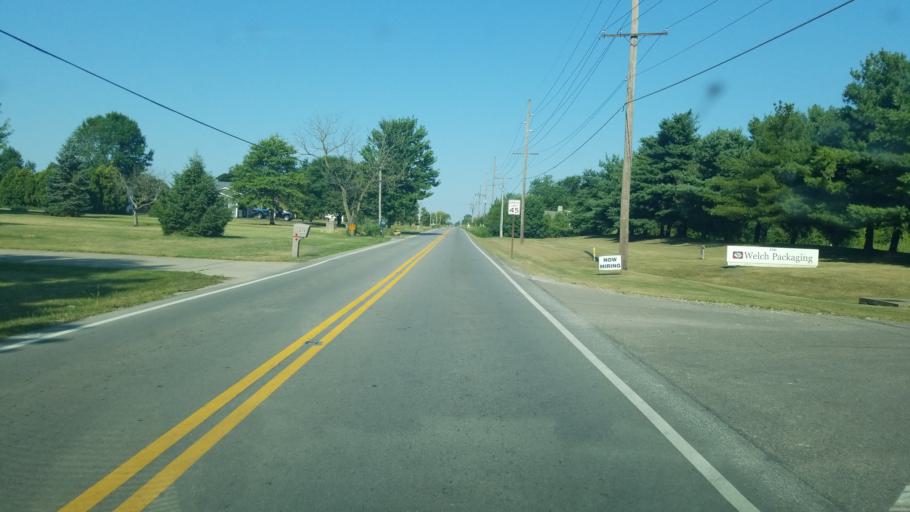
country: US
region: Ohio
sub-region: Franklin County
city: Grove City
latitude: 39.9105
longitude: -83.1207
